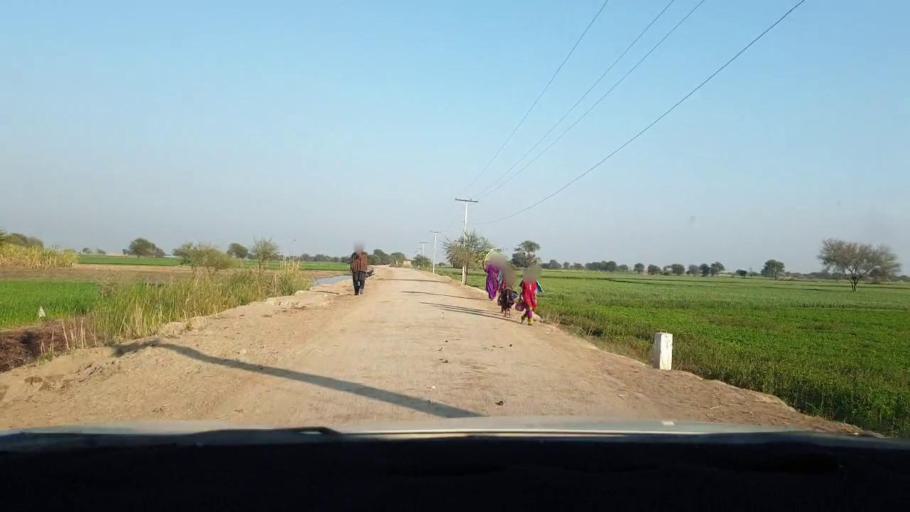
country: PK
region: Sindh
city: Berani
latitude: 25.7460
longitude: 68.7390
